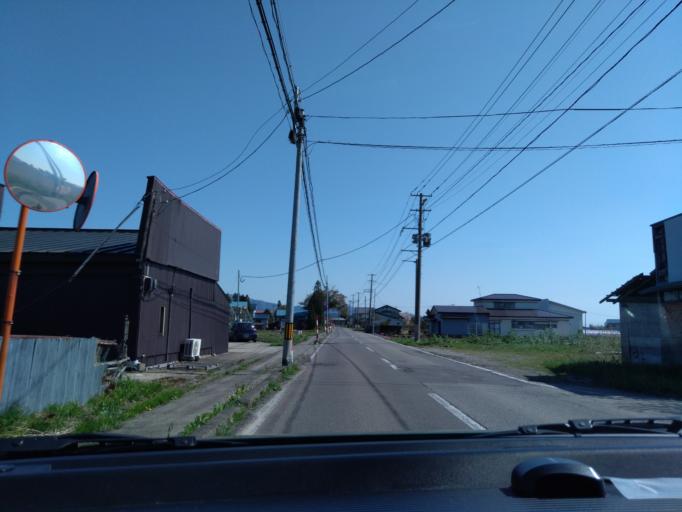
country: JP
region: Akita
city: Kakunodatemachi
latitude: 39.5200
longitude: 140.5887
